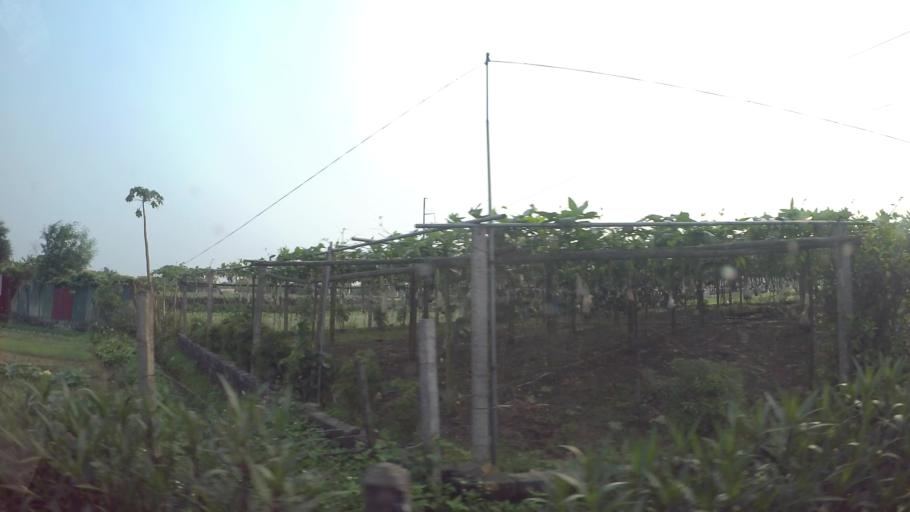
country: VN
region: Ha Noi
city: Thuong Tin
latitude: 20.8690
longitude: 105.8707
